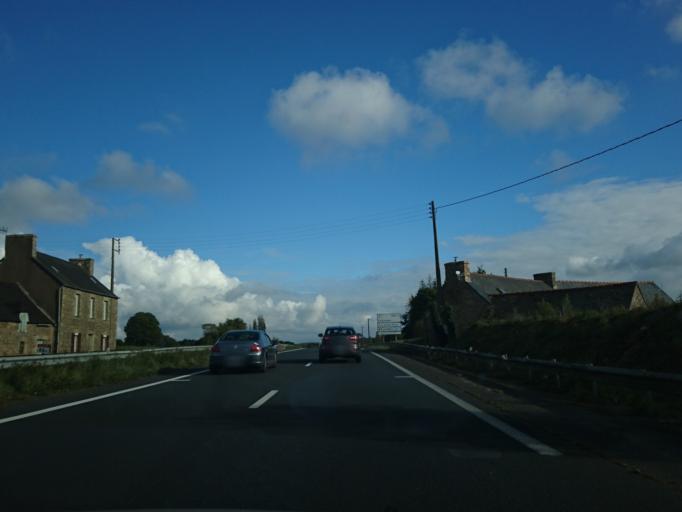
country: FR
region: Brittany
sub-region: Departement des Cotes-d'Armor
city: Saint-Agathon
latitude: 48.5495
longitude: -3.1083
